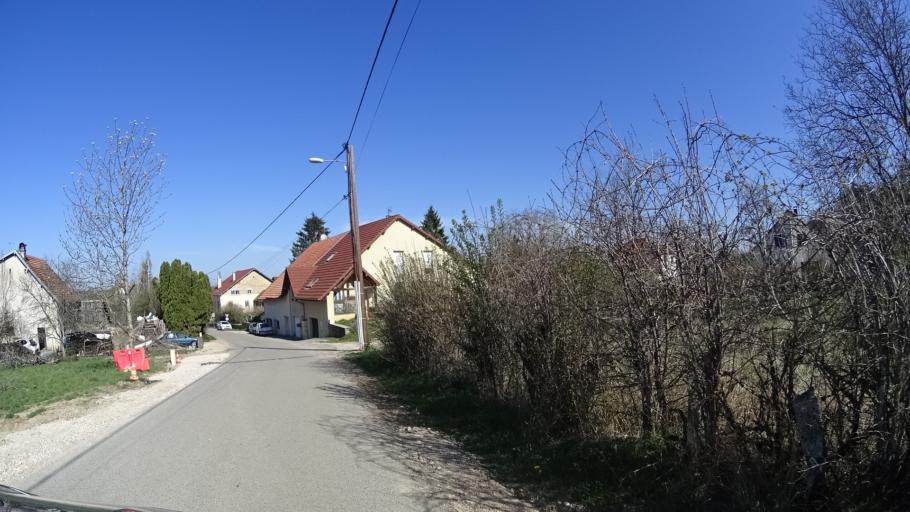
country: FR
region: Franche-Comte
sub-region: Departement du Doubs
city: Ornans
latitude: 47.1430
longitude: 6.0899
